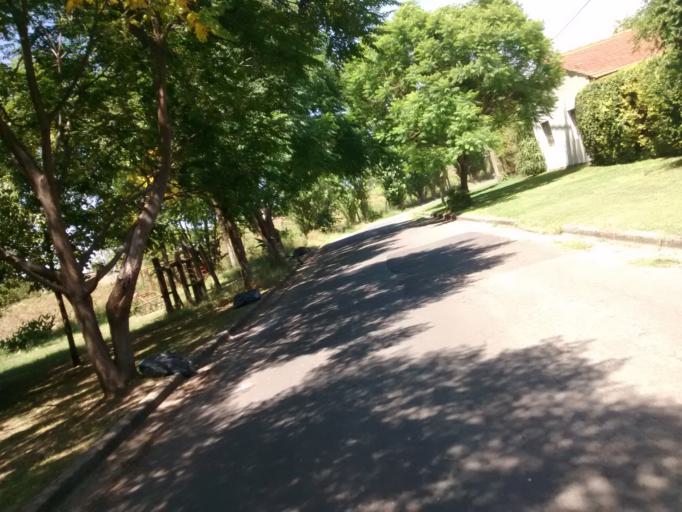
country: AR
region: Buenos Aires
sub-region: Partido de La Plata
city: La Plata
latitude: -34.8820
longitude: -58.0000
